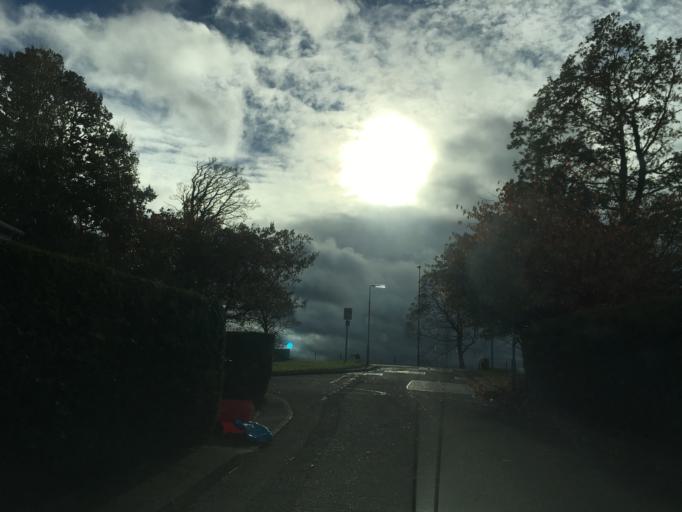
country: GB
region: Scotland
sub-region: Midlothian
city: Loanhead
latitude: 55.9003
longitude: -3.1725
